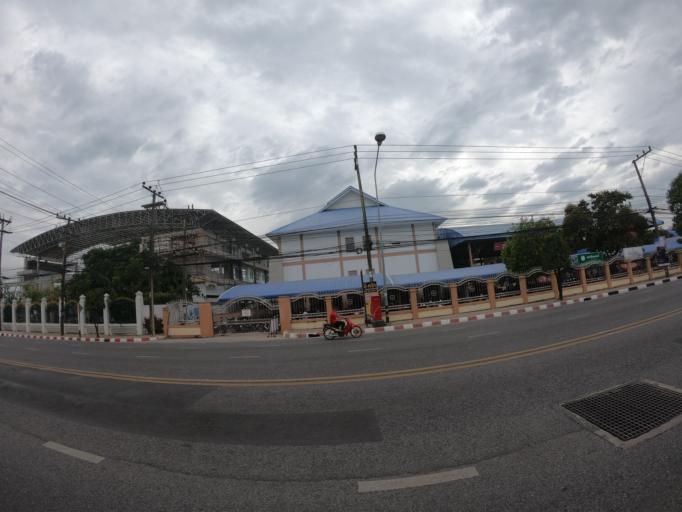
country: TH
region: Roi Et
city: Roi Et
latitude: 16.0536
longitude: 103.6560
